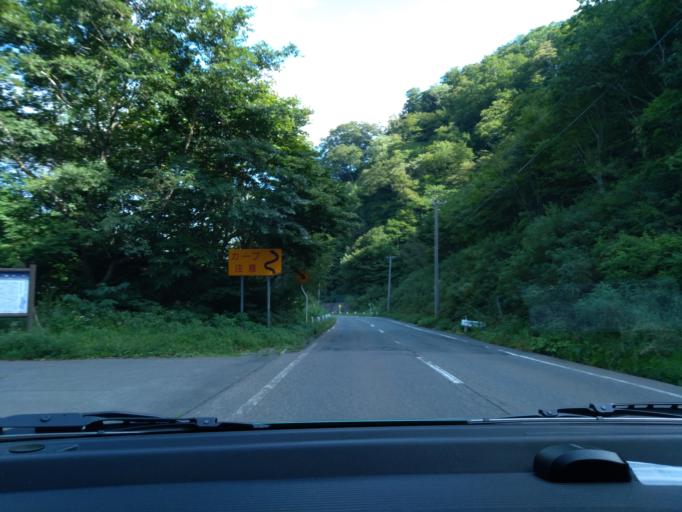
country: JP
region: Iwate
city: Shizukuishi
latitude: 39.6303
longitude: 141.0573
